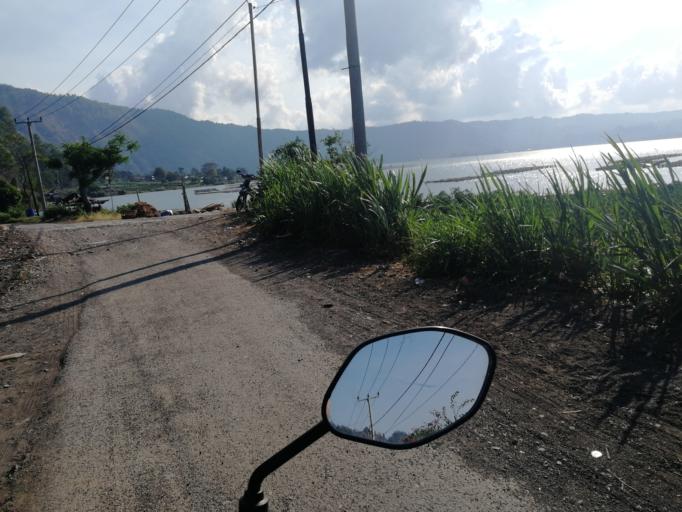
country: ID
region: Bali
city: Banjar Trunyan
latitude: -8.2656
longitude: 115.4200
